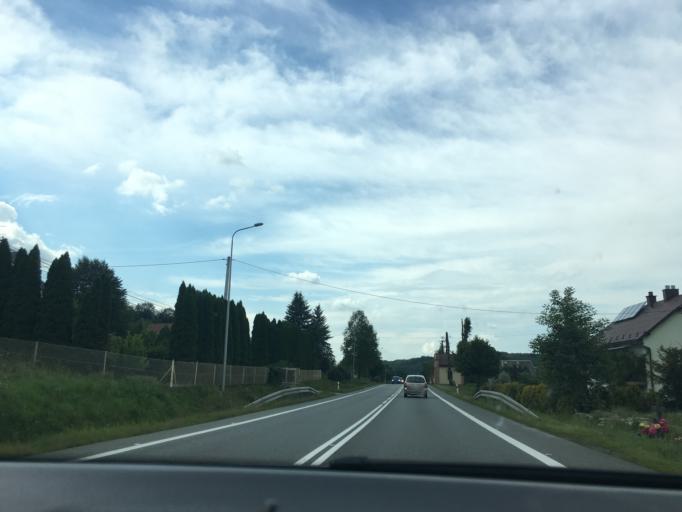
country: PL
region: Subcarpathian Voivodeship
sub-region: Powiat strzyzowski
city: Polomia
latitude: 49.8899
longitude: 21.8951
